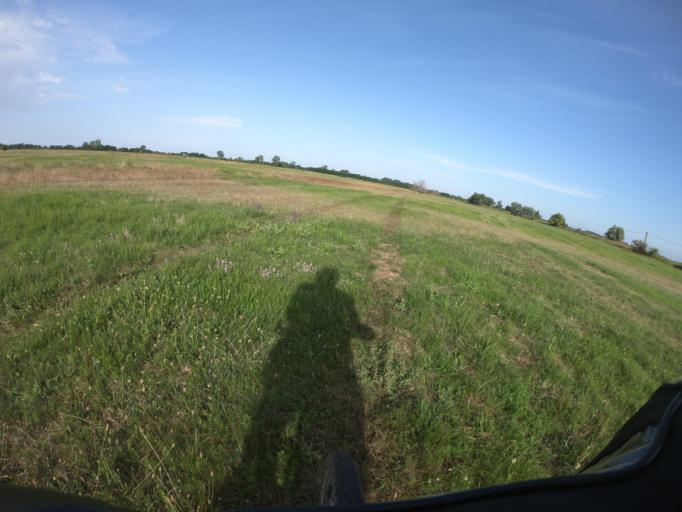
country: HU
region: Hajdu-Bihar
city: Tiszacsege
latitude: 47.6140
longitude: 21.0215
